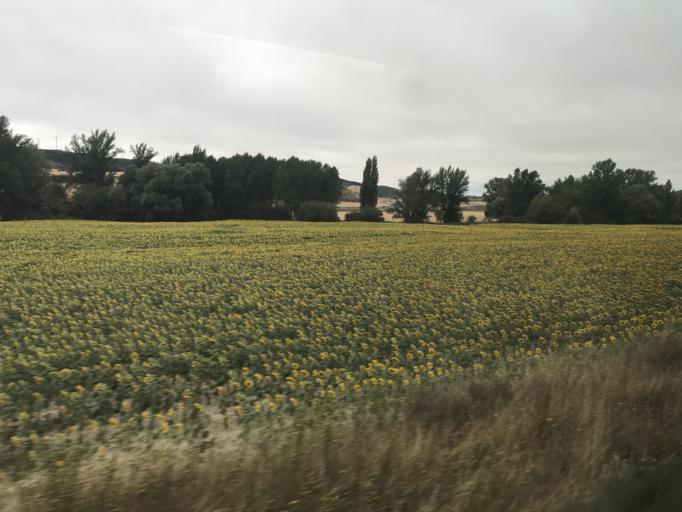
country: ES
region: Castille and Leon
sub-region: Provincia de Burgos
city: Quintanavides
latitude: 42.4824
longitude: -3.4107
